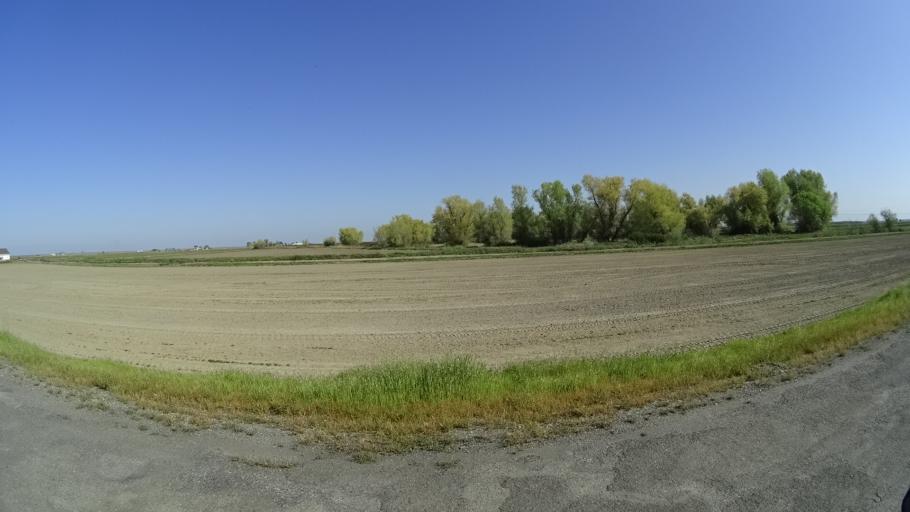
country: US
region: California
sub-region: Glenn County
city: Hamilton City
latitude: 39.6015
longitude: -122.0573
